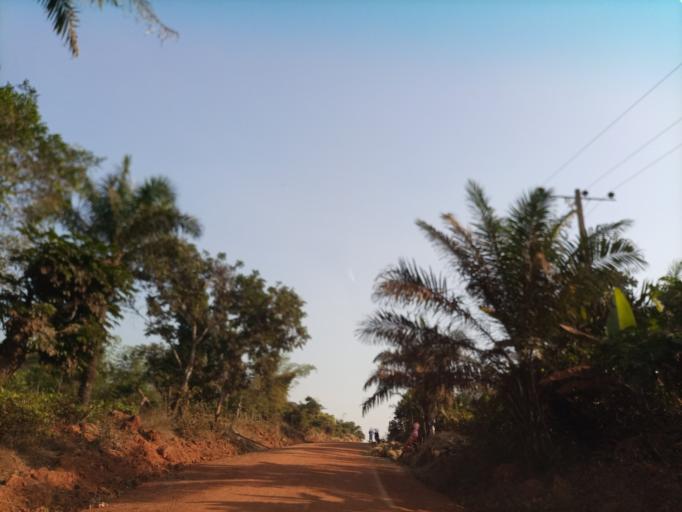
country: NG
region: Enugu
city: Opi
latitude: 6.7649
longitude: 7.3958
